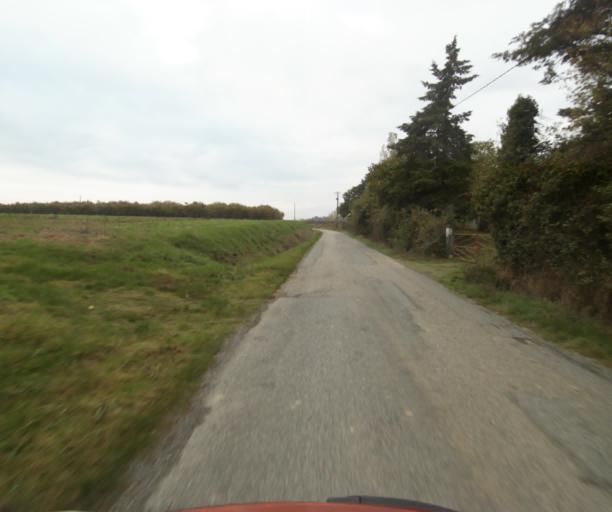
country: FR
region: Midi-Pyrenees
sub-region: Departement du Tarn-et-Garonne
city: Verdun-sur-Garonne
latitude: 43.8103
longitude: 1.2184
